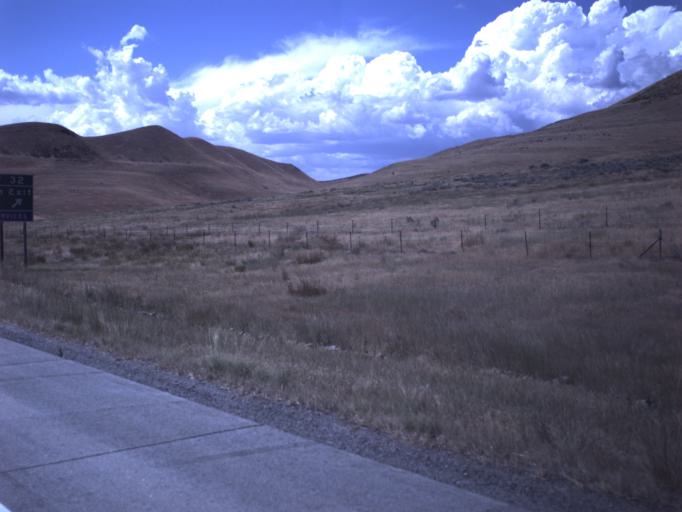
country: US
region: Utah
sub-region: Box Elder County
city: Garland
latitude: 41.7972
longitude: -112.2949
